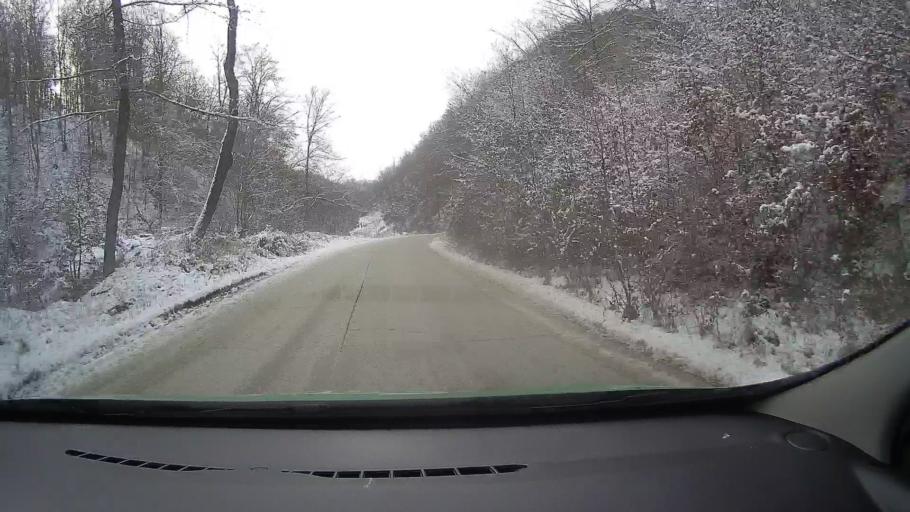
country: RO
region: Alba
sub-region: Oras Zlatna
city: Zlatna
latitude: 46.1014
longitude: 23.1898
